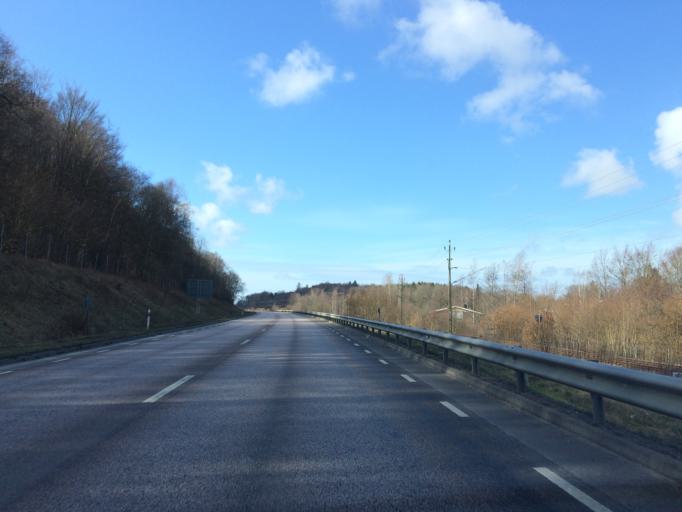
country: SE
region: Halland
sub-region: Laholms Kommun
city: Knared
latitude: 56.5165
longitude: 13.3069
